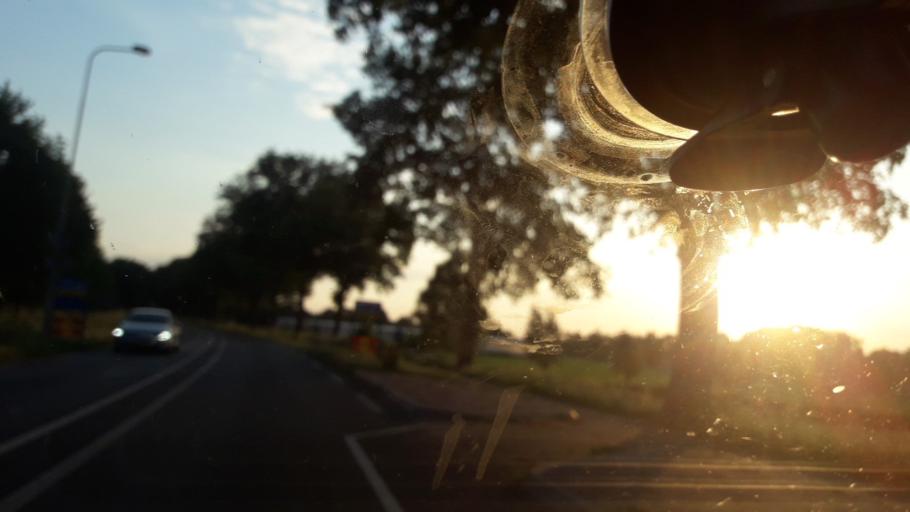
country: NL
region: Gelderland
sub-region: Gemeente Elburg
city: Elburg
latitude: 52.4433
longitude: 5.8420
